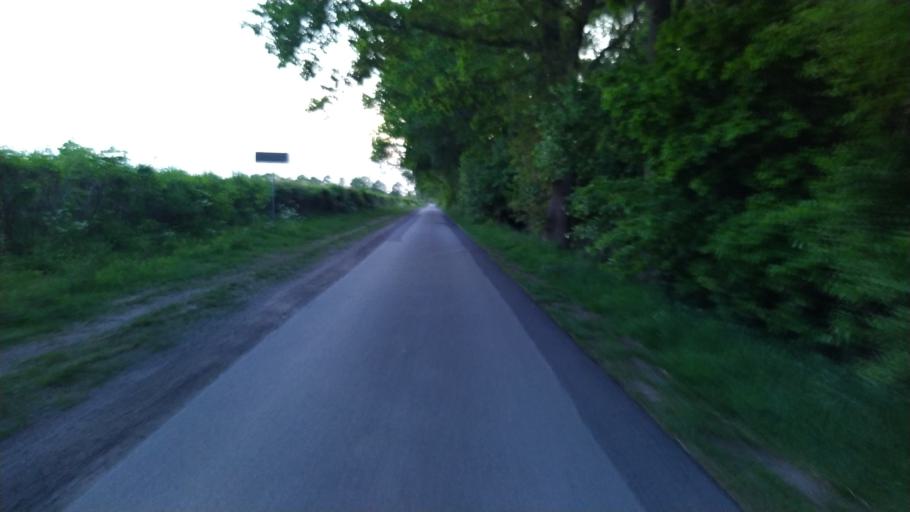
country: DE
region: Lower Saxony
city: Bargstedt
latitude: 53.4824
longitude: 9.4644
